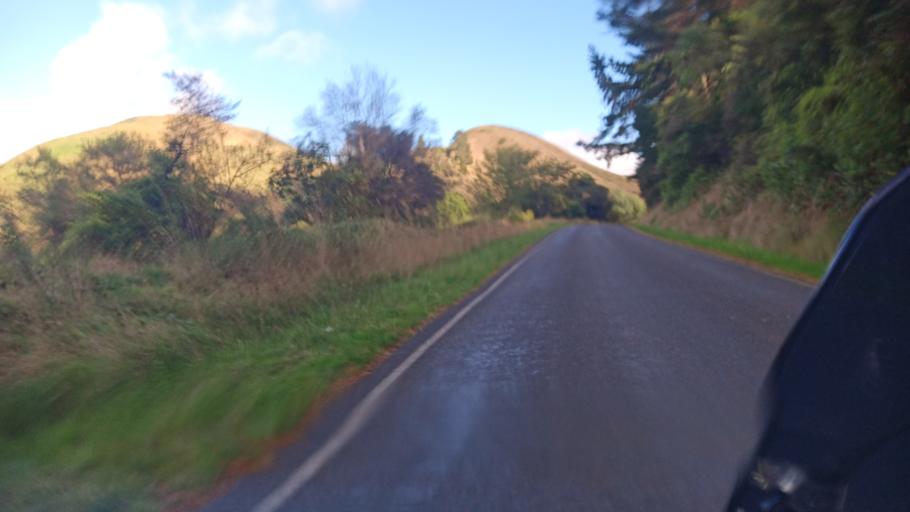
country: NZ
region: Gisborne
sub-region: Gisborne District
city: Gisborne
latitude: -38.5395
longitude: 177.5629
